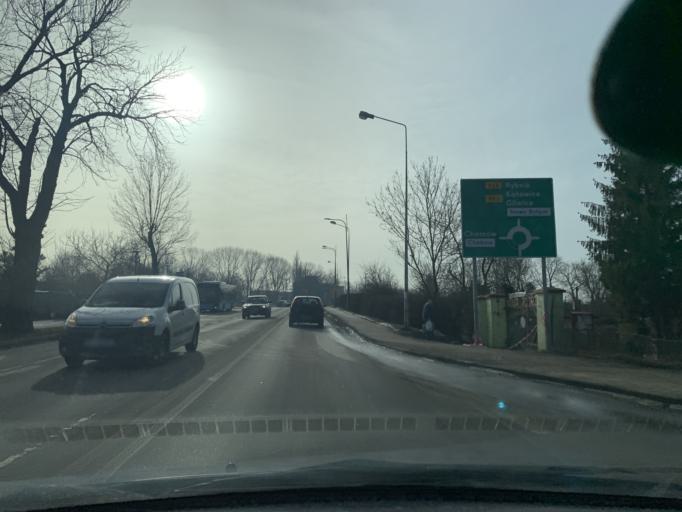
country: PL
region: Silesian Voivodeship
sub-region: Ruda Slaska
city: Ruda Slaska
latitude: 50.3079
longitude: 18.8532
